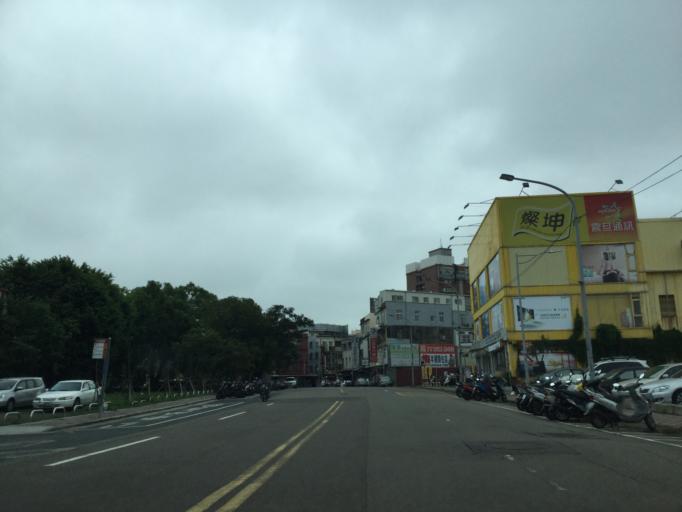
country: TW
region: Taiwan
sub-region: Hsinchu
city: Hsinchu
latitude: 24.7954
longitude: 121.0019
